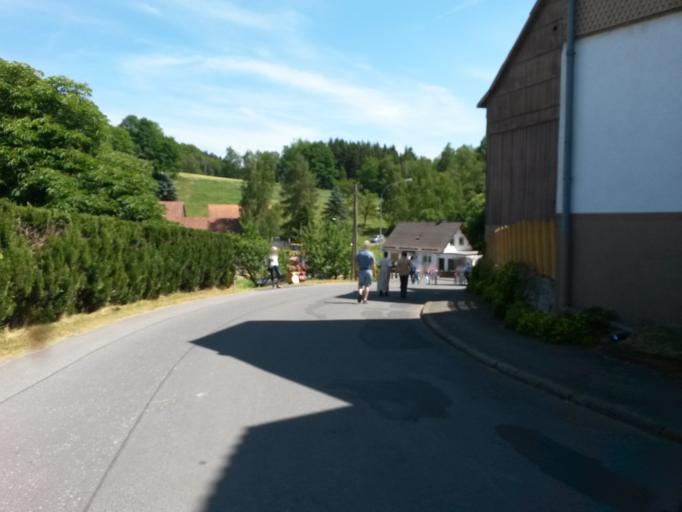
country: DE
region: Hesse
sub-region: Regierungsbezirk Kassel
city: Hilders
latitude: 50.5526
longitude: 9.9348
